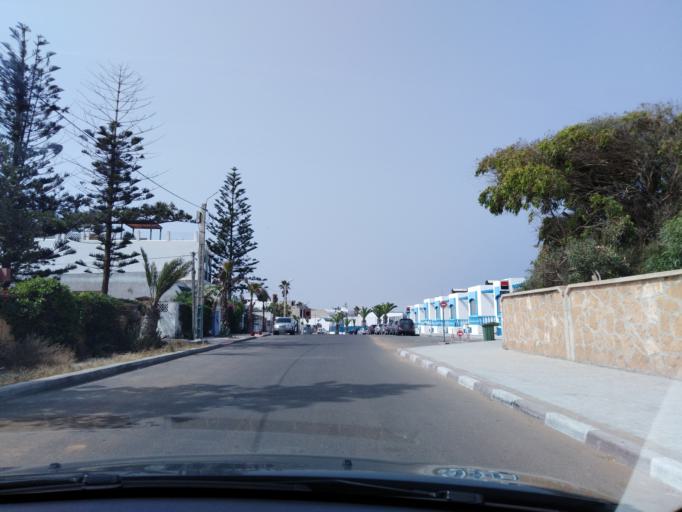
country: MA
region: Doukkala-Abda
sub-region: Safi
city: Safi
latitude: 32.7327
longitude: -9.0459
